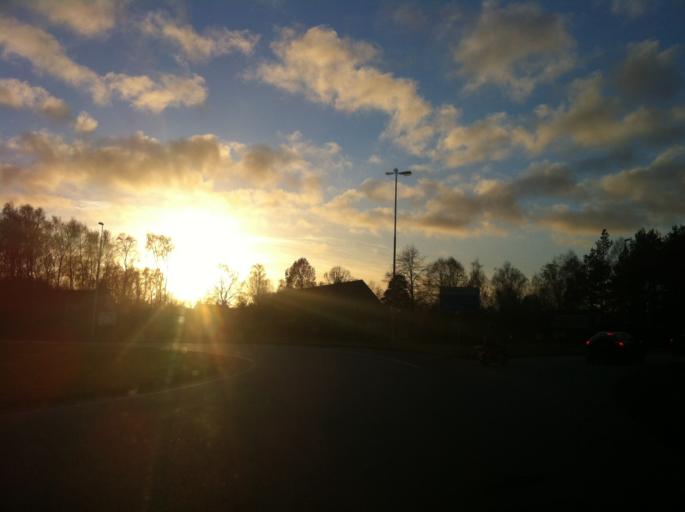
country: SE
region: Skane
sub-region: Hoors Kommun
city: Hoeoer
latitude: 55.9431
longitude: 13.5603
